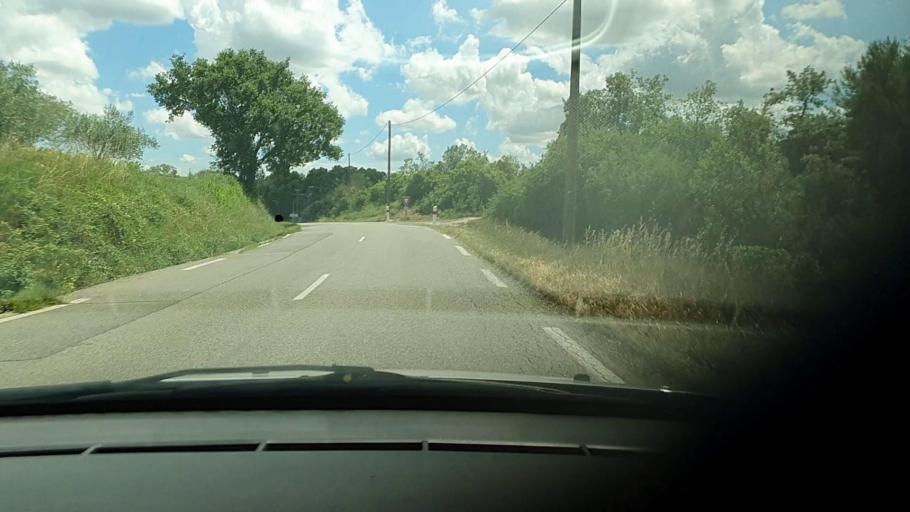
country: FR
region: Languedoc-Roussillon
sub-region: Departement du Gard
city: Moussac
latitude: 44.0568
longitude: 4.2227
